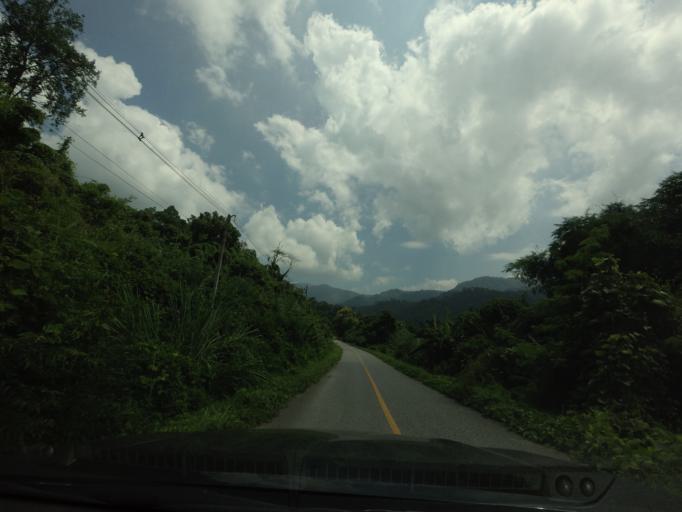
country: TH
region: Loei
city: Na Haeo
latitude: 17.6989
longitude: 100.9432
